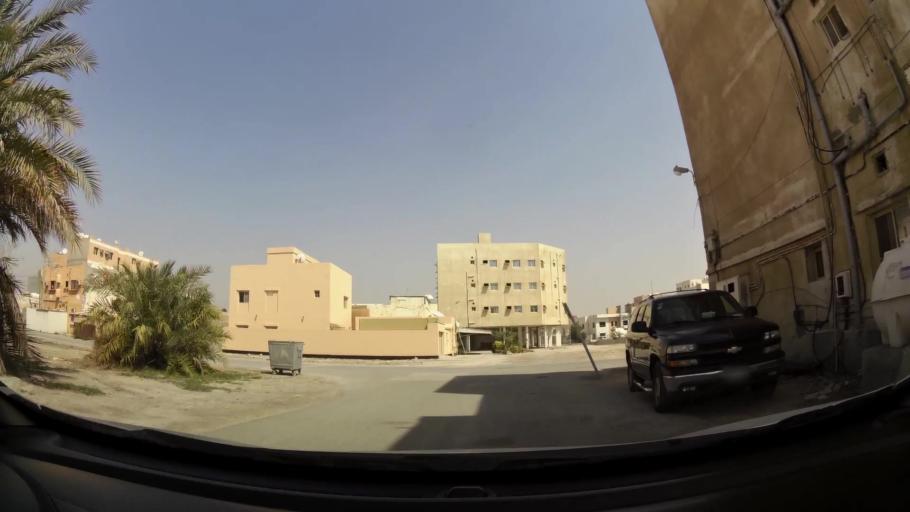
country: BH
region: Manama
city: Jidd Hafs
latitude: 26.2109
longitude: 50.4492
